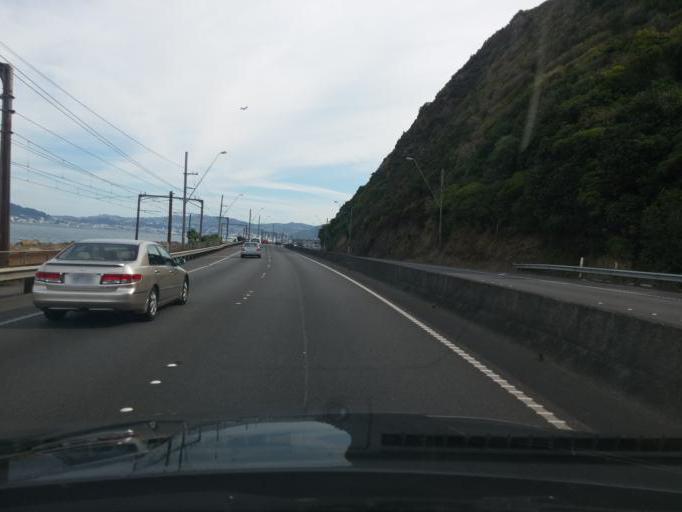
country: NZ
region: Wellington
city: Petone
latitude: -41.2387
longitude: 174.8280
